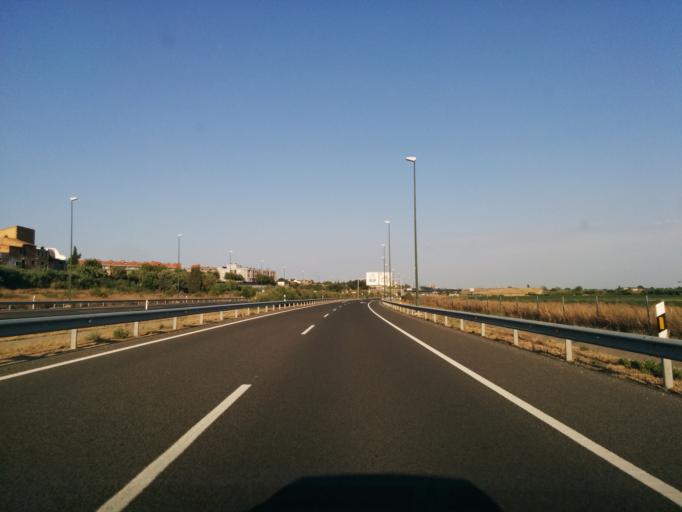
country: ES
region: Aragon
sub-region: Provincia de Zaragoza
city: Zaragoza
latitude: 41.6649
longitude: -0.8297
